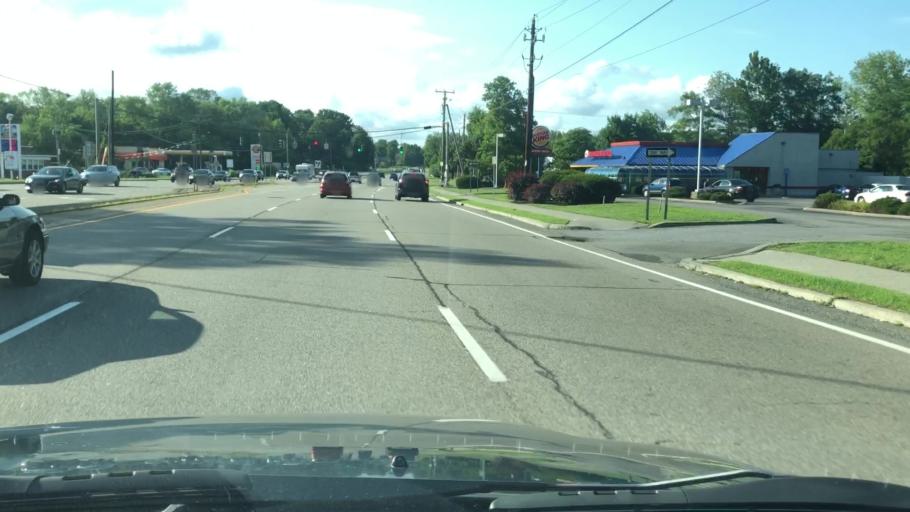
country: US
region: New York
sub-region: Dutchess County
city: Fishkill
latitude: 41.5368
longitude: -73.8997
